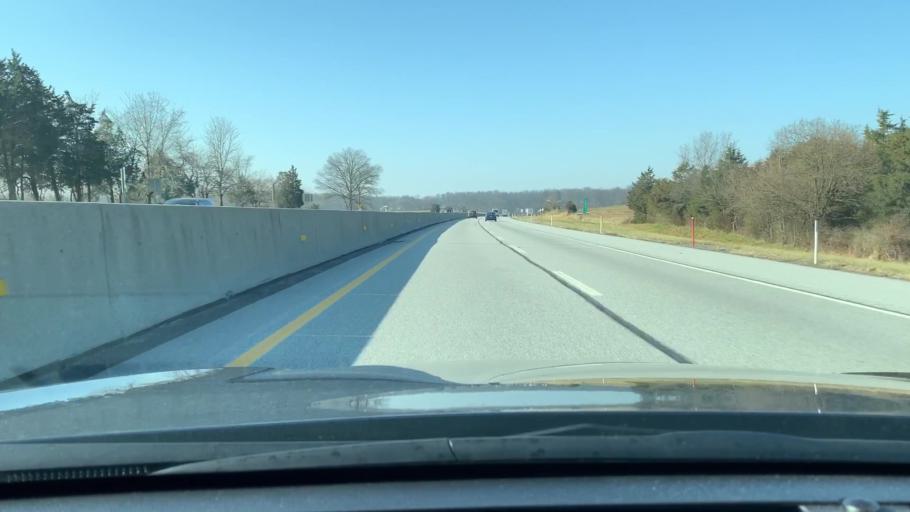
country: US
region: Pennsylvania
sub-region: Lancaster County
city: Elizabethtown
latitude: 40.2076
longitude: -76.6035
